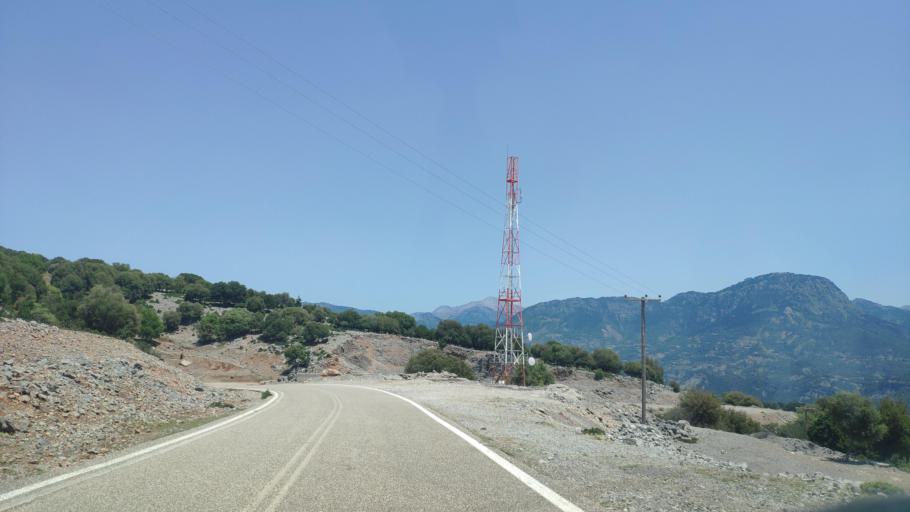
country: GR
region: Central Greece
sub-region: Nomos Evrytanias
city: Kerasochori
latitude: 39.0821
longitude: 21.4106
